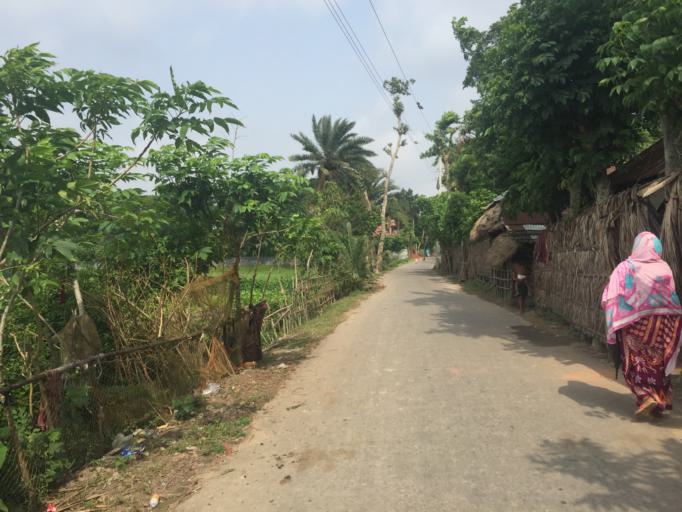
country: BD
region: Barisal
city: Mathba
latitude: 22.2140
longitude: 89.9202
